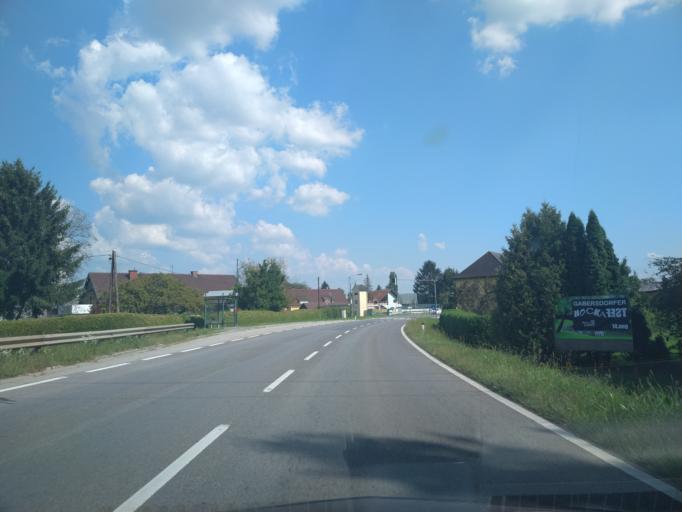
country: AT
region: Styria
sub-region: Politischer Bezirk Leibnitz
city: Gabersdorf
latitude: 46.7655
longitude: 15.5776
